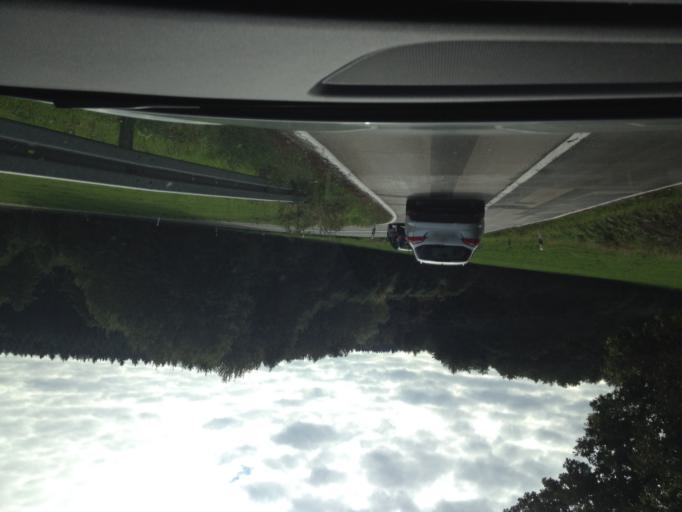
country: DE
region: Saarland
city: Mainzweiler
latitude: 49.4052
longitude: 7.1123
